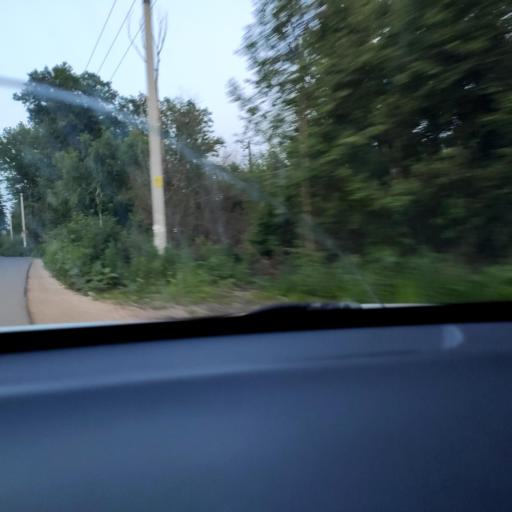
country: RU
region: Tatarstan
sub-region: Gorod Kazan'
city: Kazan
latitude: 55.8474
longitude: 49.1690
